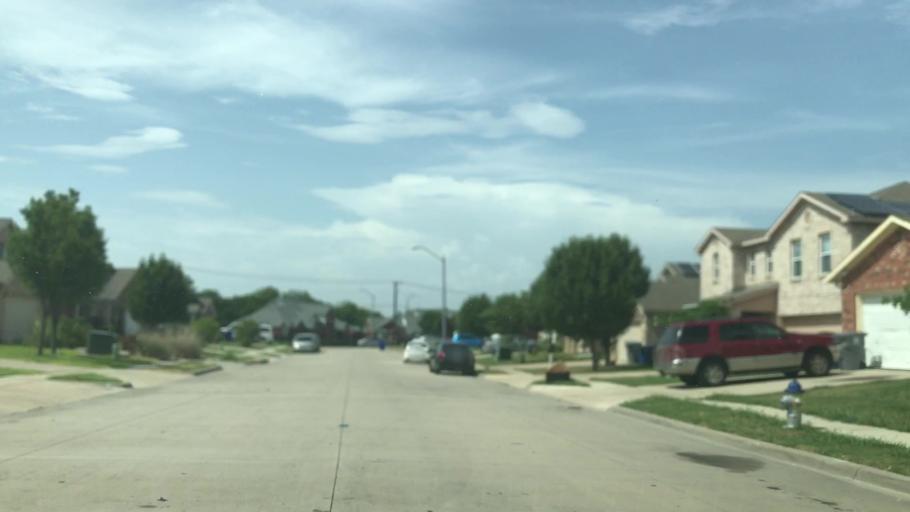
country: US
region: Texas
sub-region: Dallas County
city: Cockrell Hill
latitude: 32.7847
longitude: -96.8708
